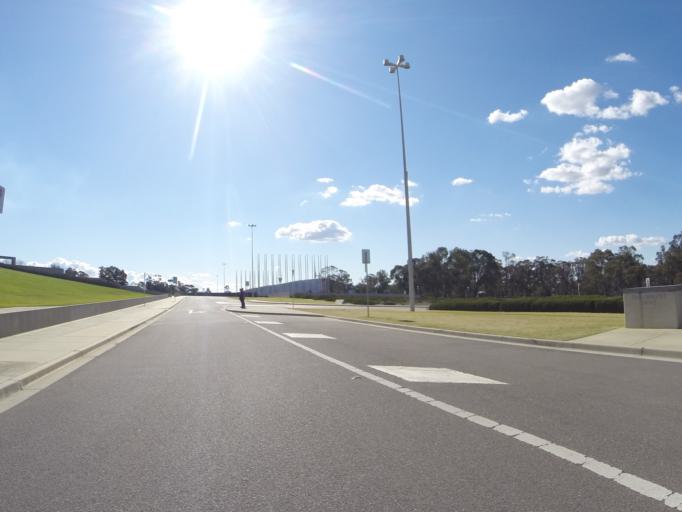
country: AU
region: Australian Capital Territory
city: Forrest
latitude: -35.3076
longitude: 149.1274
